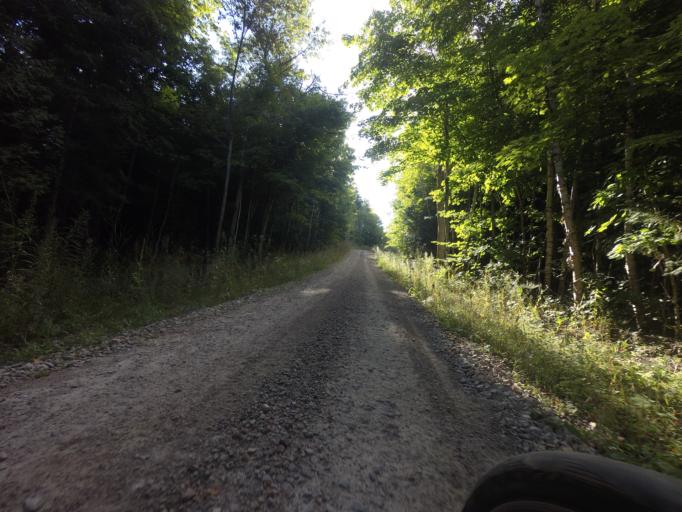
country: CA
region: Ontario
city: Arnprior
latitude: 45.1915
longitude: -76.5206
